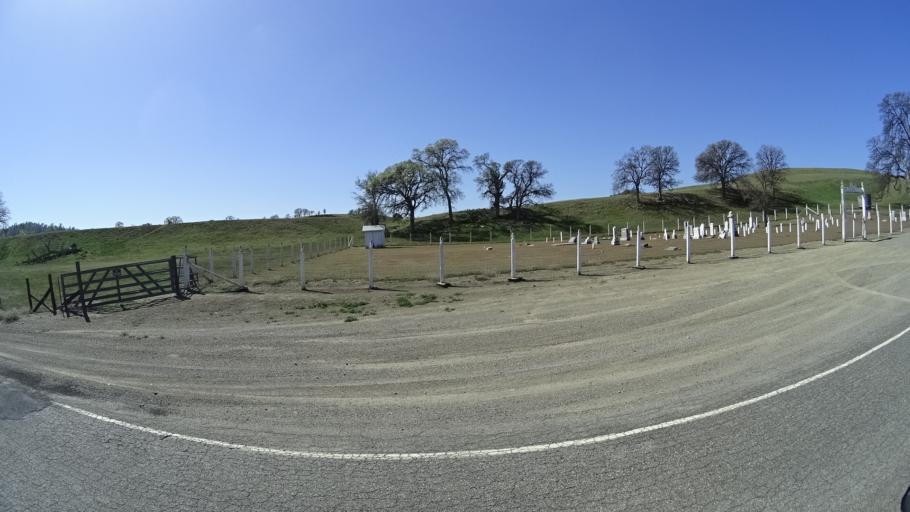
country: US
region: California
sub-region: Glenn County
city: Orland
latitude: 39.6811
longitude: -122.5337
